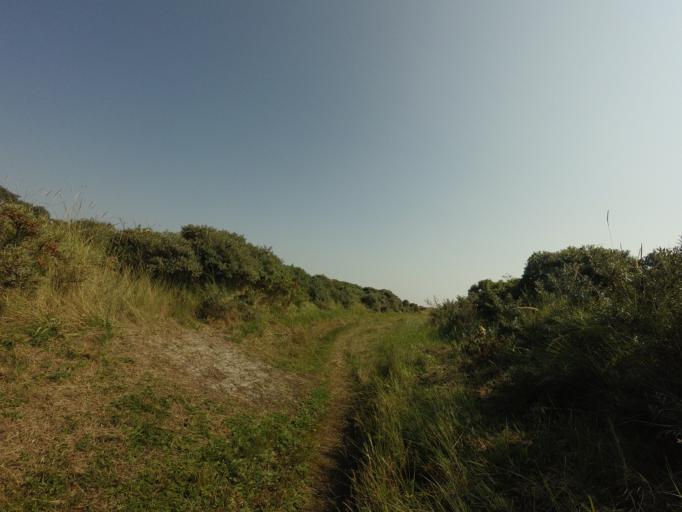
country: NL
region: Friesland
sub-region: Gemeente Schiermonnikoog
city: Schiermonnikoog
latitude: 53.4961
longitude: 6.2419
